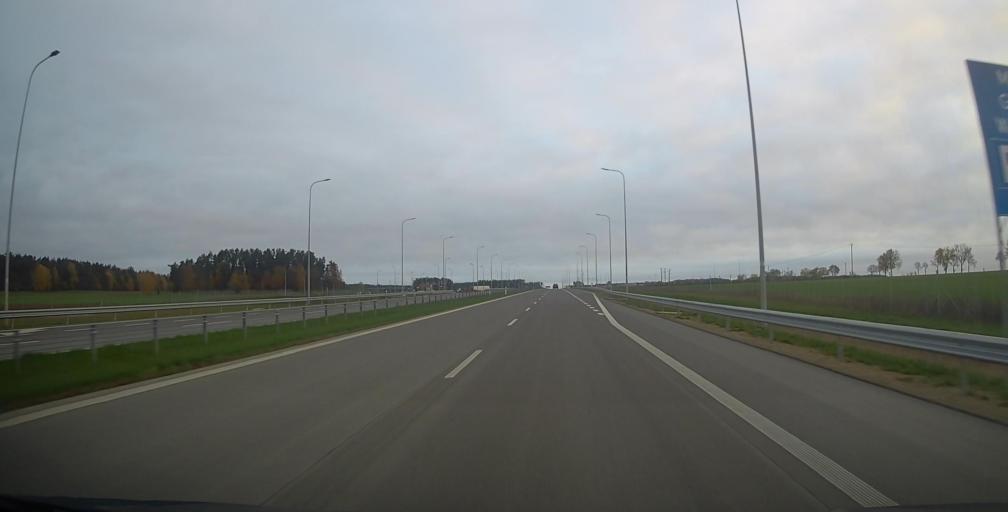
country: PL
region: Podlasie
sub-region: Powiat lomzynski
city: Piatnica
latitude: 53.2668
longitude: 22.1227
